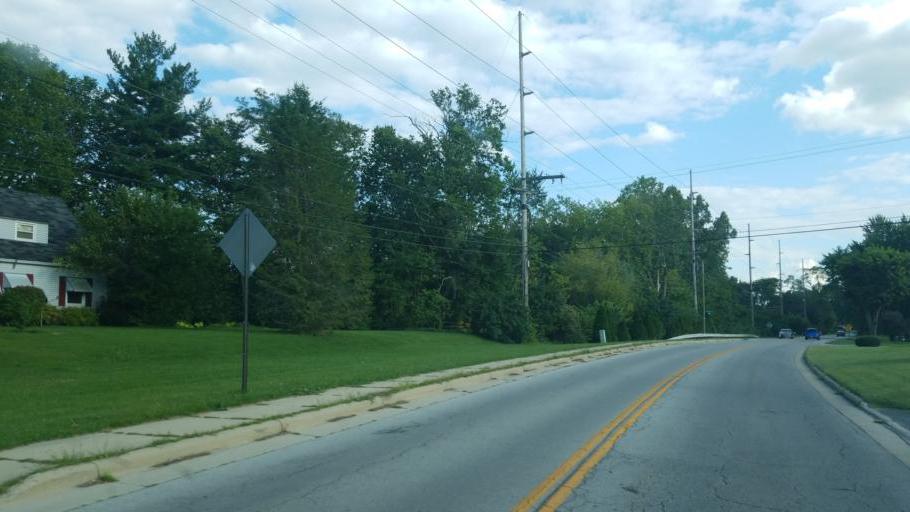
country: US
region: Ohio
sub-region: Sandusky County
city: Ballville
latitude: 41.3257
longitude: -83.1300
